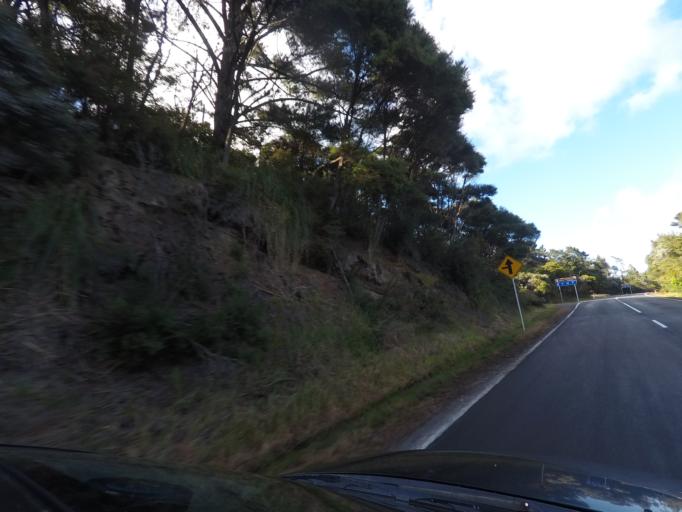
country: NZ
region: Auckland
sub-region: Auckland
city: Titirangi
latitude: -36.9932
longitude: 174.6020
